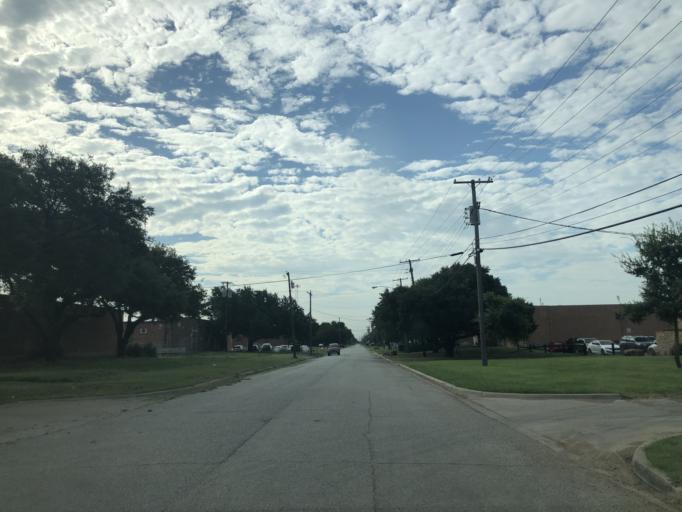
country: US
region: Texas
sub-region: Dallas County
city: Irving
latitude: 32.8224
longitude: -96.8899
